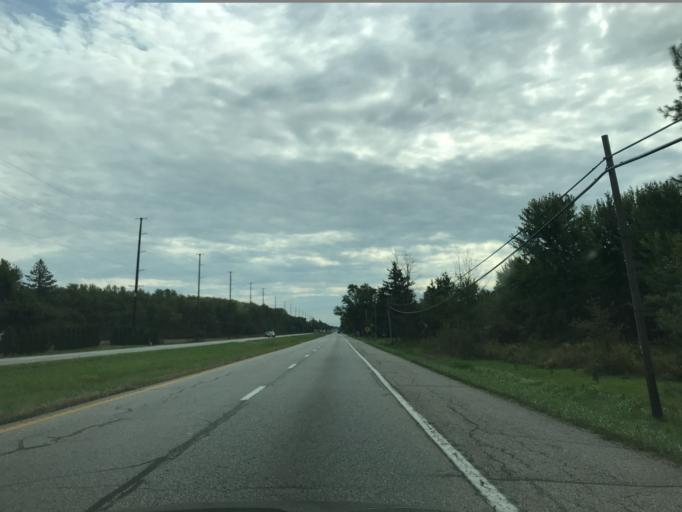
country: US
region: Ohio
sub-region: Trumbull County
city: Leavittsburg
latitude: 41.2787
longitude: -80.9093
